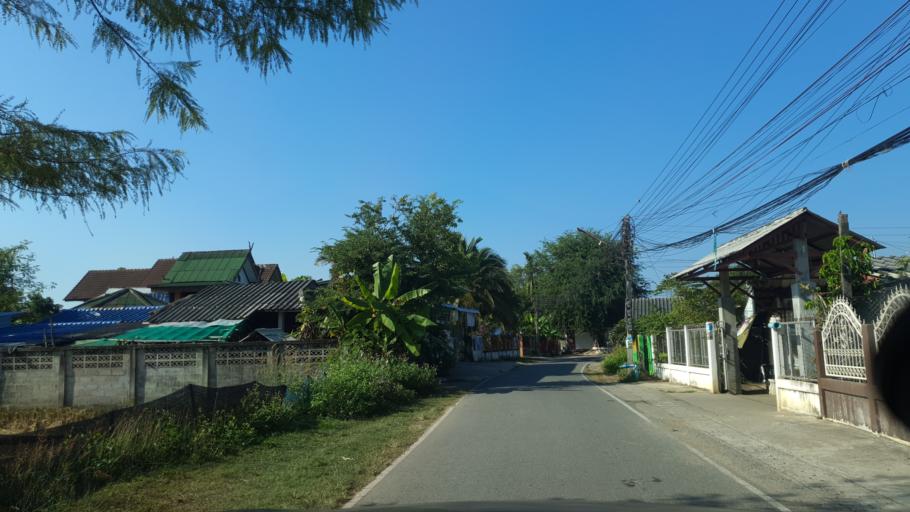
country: TH
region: Chiang Mai
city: San Kamphaeng
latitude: 18.7340
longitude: 99.1490
